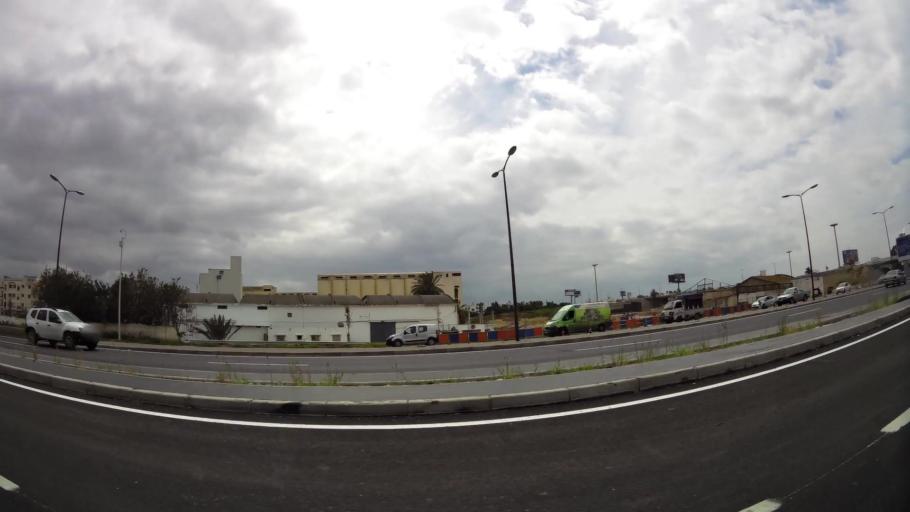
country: MA
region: Grand Casablanca
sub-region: Casablanca
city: Casablanca
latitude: 33.5499
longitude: -7.6420
